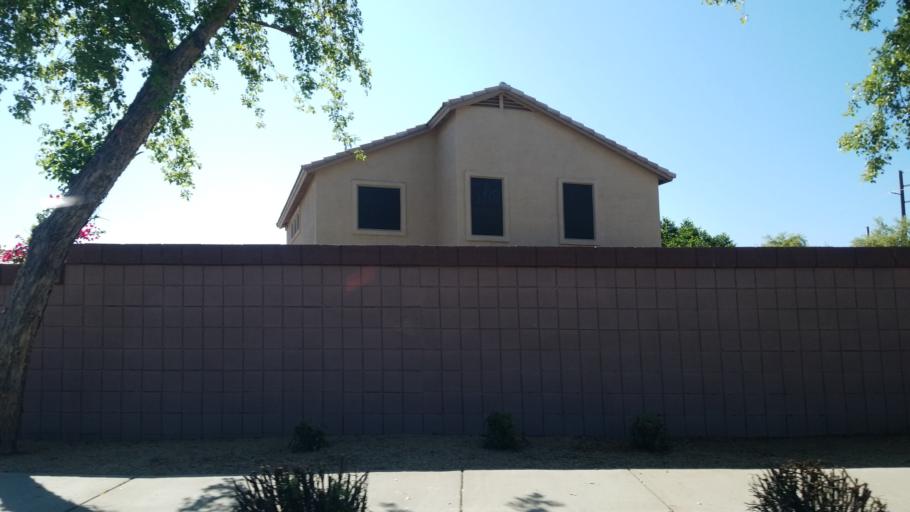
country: US
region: Arizona
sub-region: Maricopa County
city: Glendale
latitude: 33.5526
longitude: -112.1733
